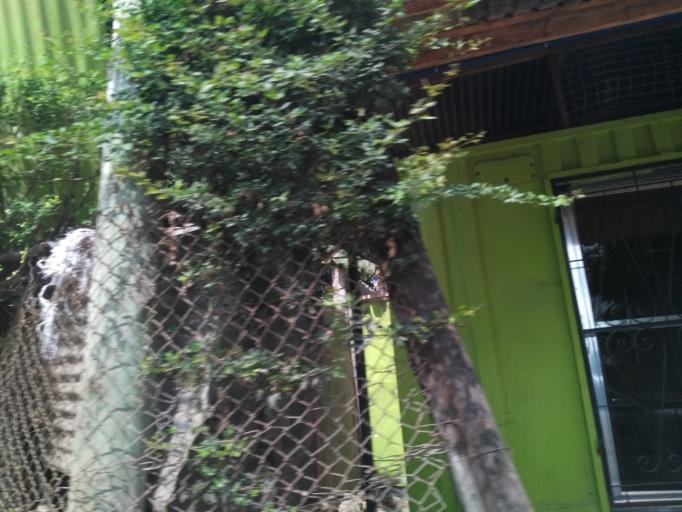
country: TZ
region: Dar es Salaam
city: Magomeni
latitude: -6.7778
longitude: 39.2720
